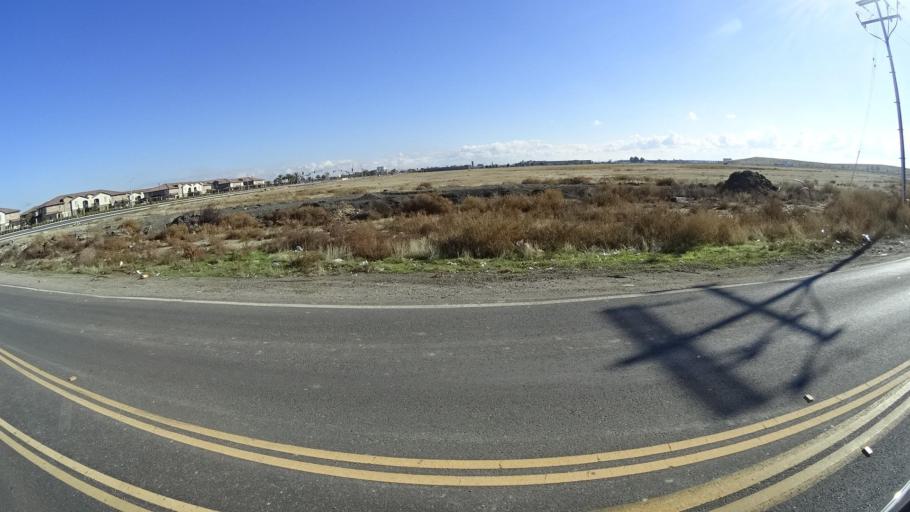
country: US
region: California
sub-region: Kern County
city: Delano
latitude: 35.7461
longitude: -119.2584
